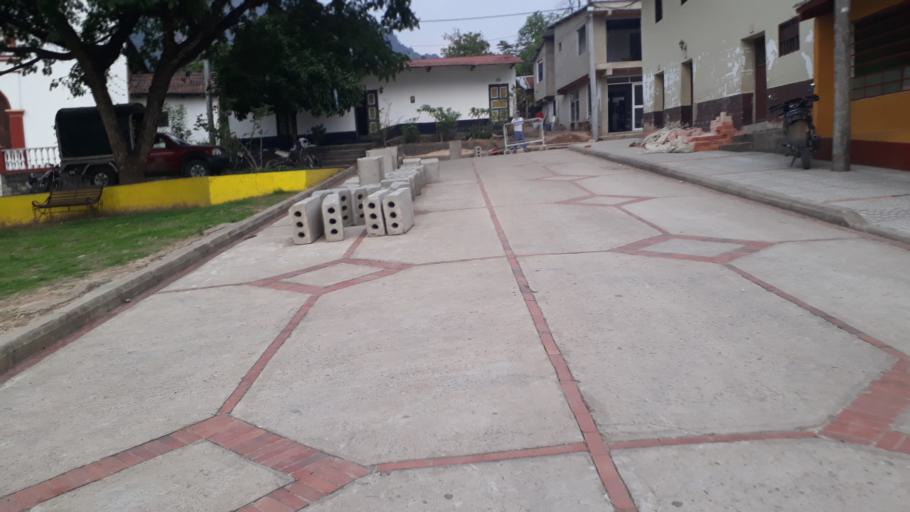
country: CO
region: Casanare
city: Nunchia
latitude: 5.6246
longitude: -72.4234
